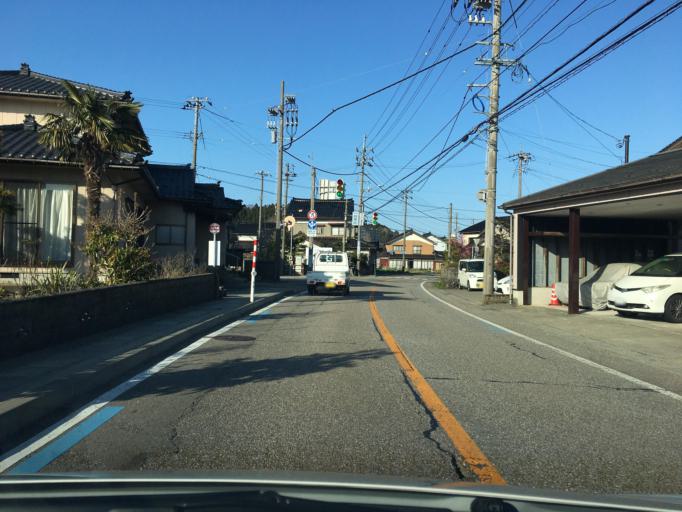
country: JP
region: Toyama
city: Himi
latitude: 36.8820
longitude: 136.9901
